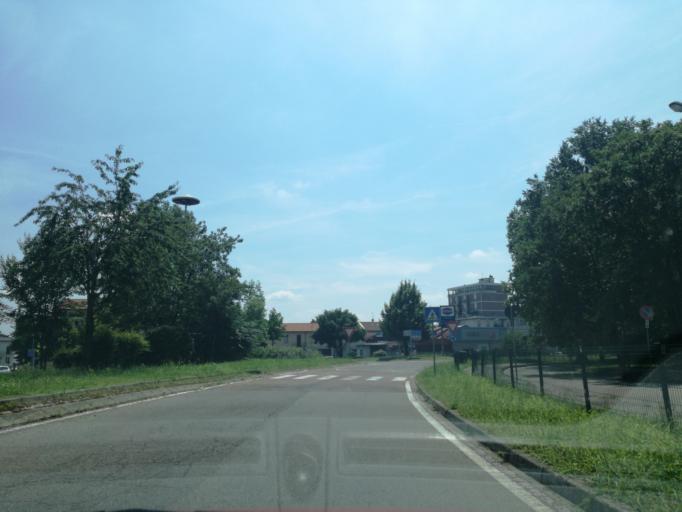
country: IT
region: Lombardy
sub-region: Provincia di Monza e Brianza
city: Desio
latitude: 45.6272
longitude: 9.2062
